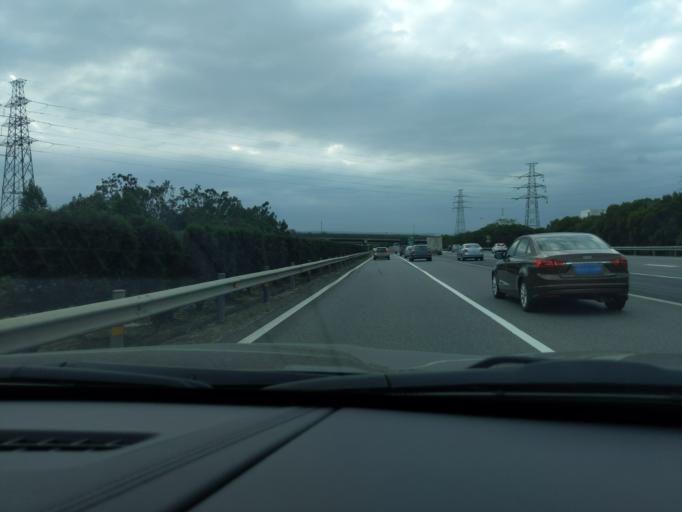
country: CN
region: Fujian
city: Maxiang
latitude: 24.6918
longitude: 118.2367
